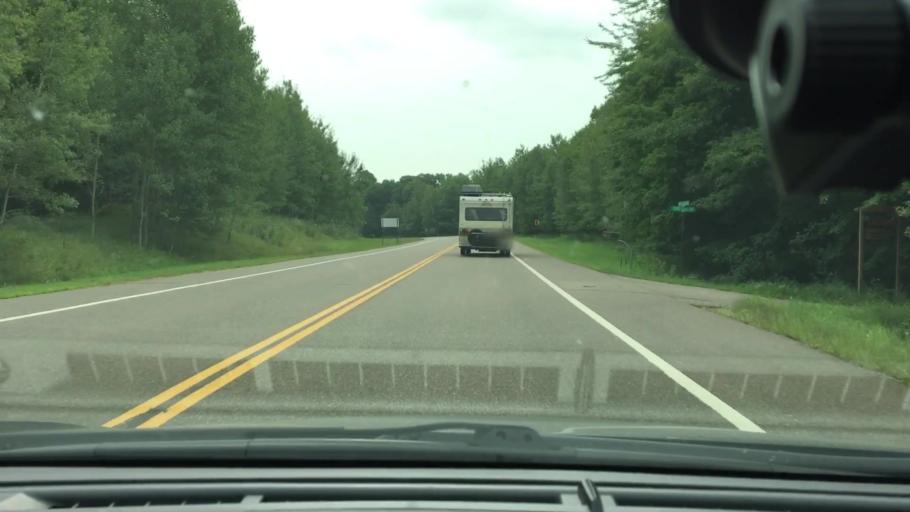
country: US
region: Minnesota
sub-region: Crow Wing County
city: Crosby
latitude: 46.4099
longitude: -93.8239
